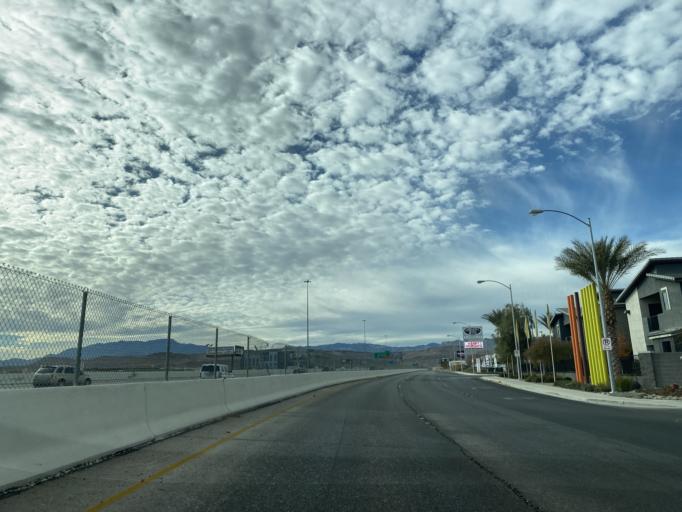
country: US
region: Nevada
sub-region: Clark County
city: Spring Valley
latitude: 36.0667
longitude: -115.2641
